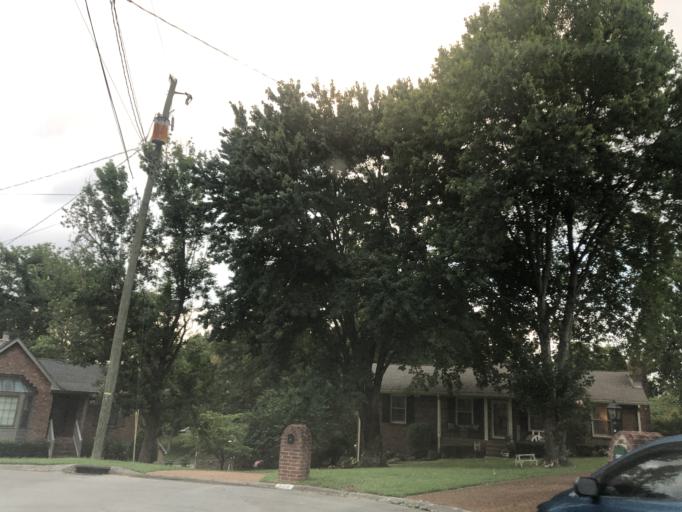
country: US
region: Tennessee
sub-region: Davidson County
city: Lakewood
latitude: 36.1477
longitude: -86.6333
